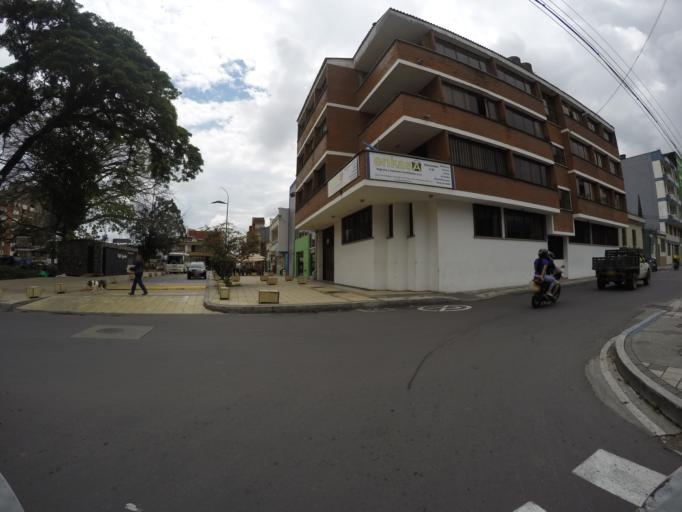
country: CO
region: Quindio
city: Armenia
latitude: 4.5360
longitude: -75.6686
